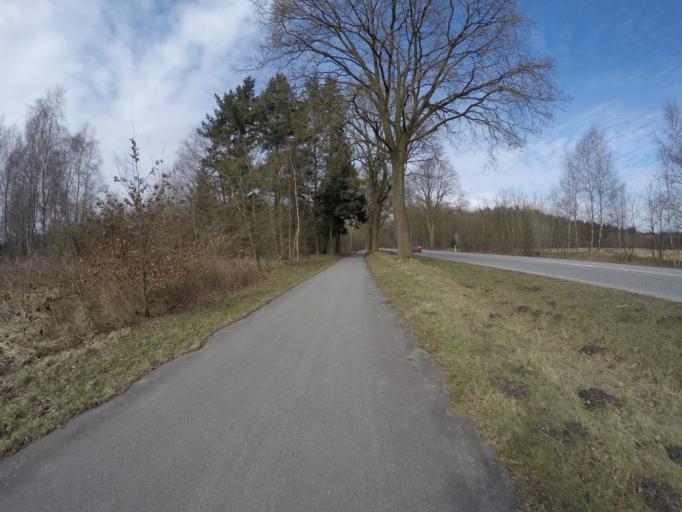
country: DE
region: Schleswig-Holstein
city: Langeln
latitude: 53.8147
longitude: 9.8805
